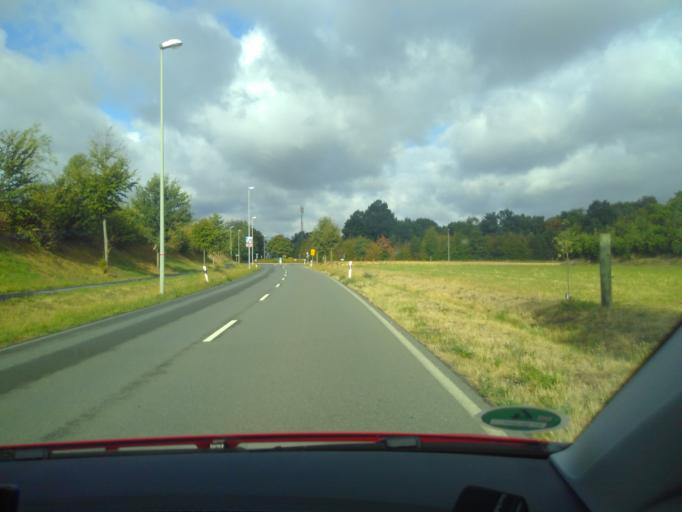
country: DE
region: North Rhine-Westphalia
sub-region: Regierungsbezirk Munster
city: Warendorf
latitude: 51.9633
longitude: 8.0011
